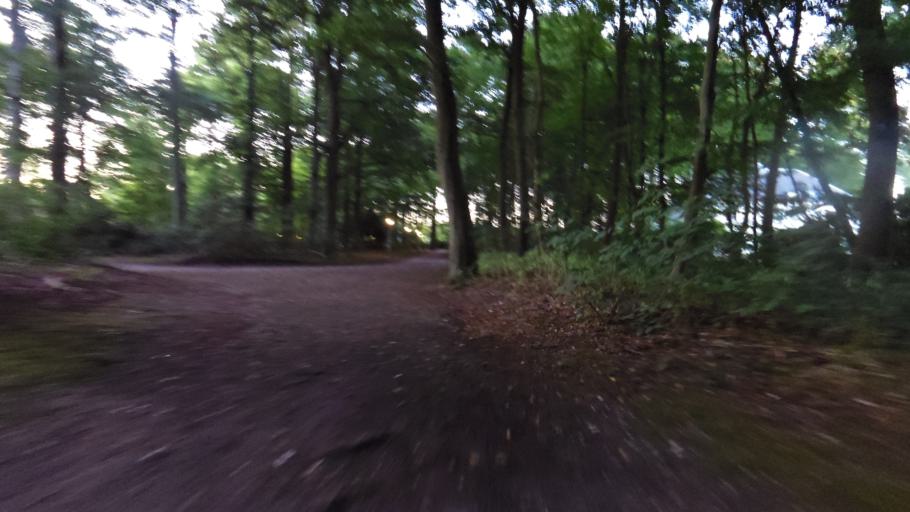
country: NL
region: Utrecht
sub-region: Gemeente Soest
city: Soest
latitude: 52.1641
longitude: 5.2411
